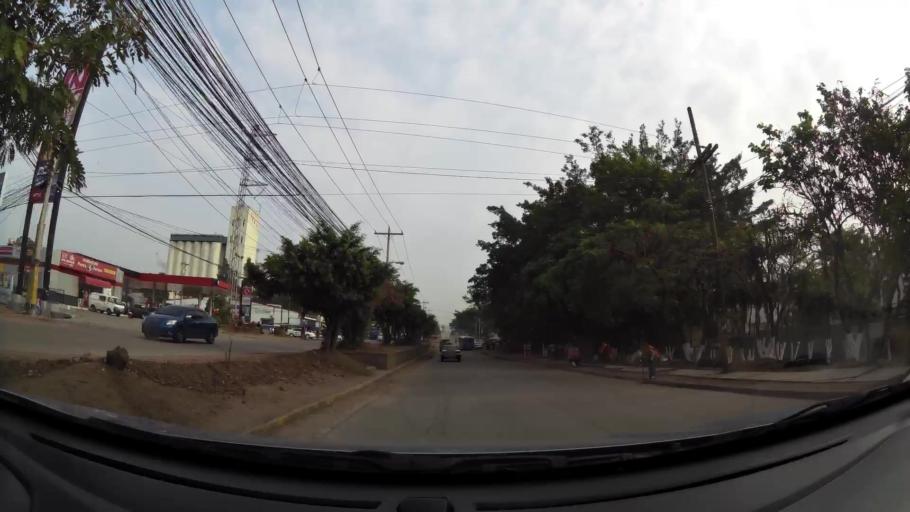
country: HN
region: Francisco Morazan
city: El Tablon
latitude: 14.0600
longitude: -87.1821
